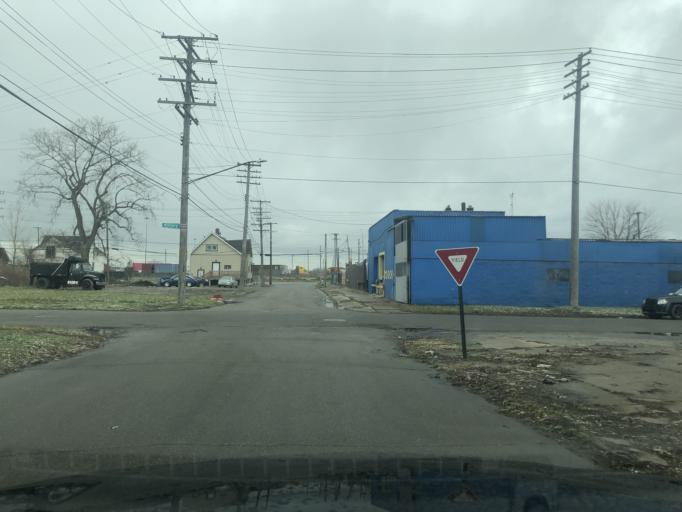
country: US
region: Michigan
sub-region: Wayne County
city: River Rouge
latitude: 42.3235
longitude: -83.1129
